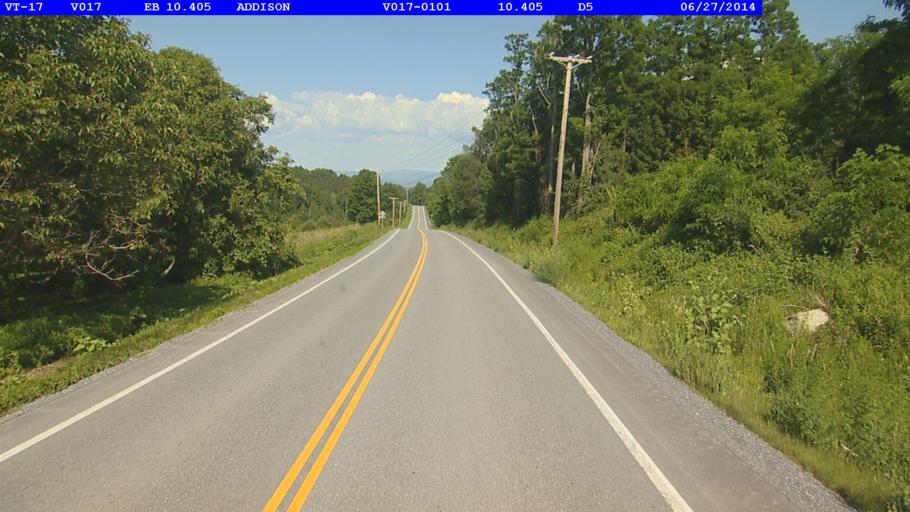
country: US
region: Vermont
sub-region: Addison County
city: Vergennes
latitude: 44.0824
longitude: -73.2645
